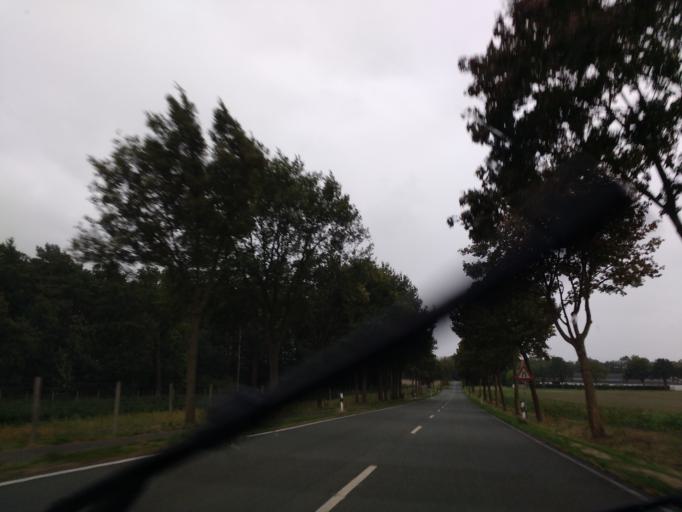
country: DE
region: North Rhine-Westphalia
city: Rietberg
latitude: 51.7430
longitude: 8.4475
